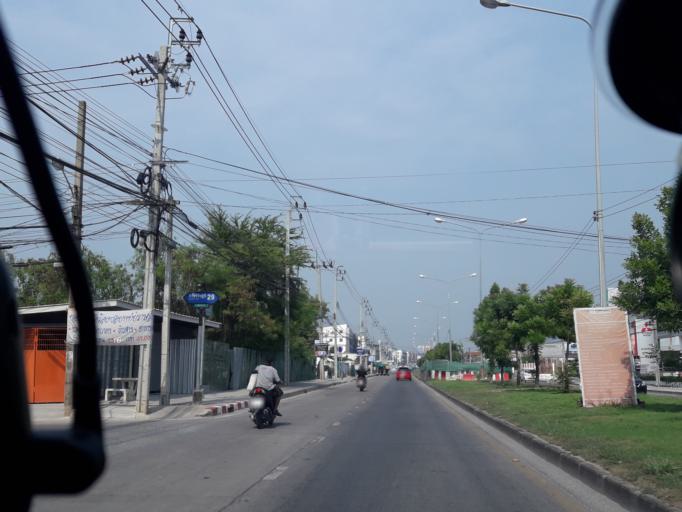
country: TH
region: Bangkok
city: Khlong Sam Wa
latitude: 13.8313
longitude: 100.7201
